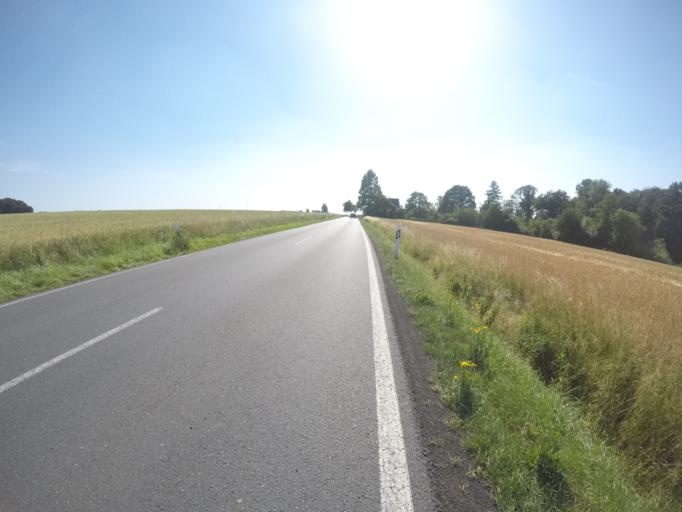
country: DE
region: North Rhine-Westphalia
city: Loehne
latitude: 52.1761
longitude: 8.7379
